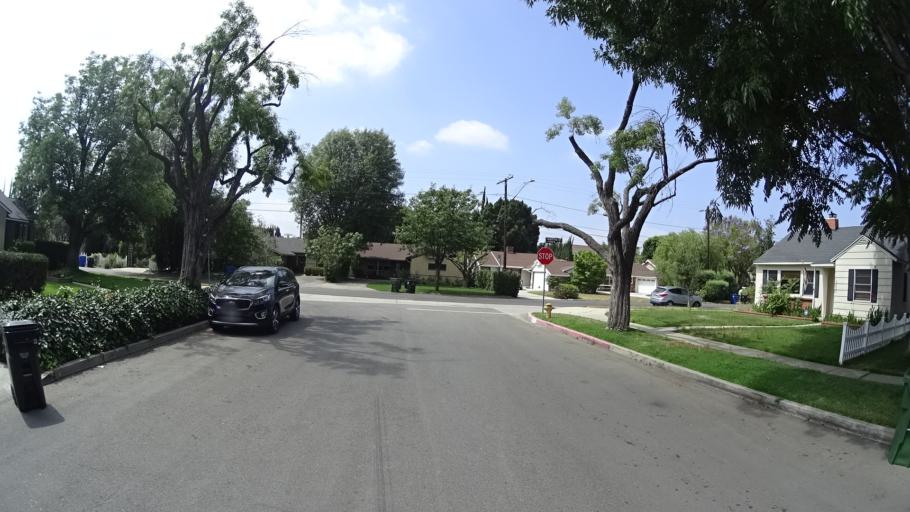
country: US
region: California
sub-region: Los Angeles County
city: Van Nuys
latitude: 34.1733
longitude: -118.4607
